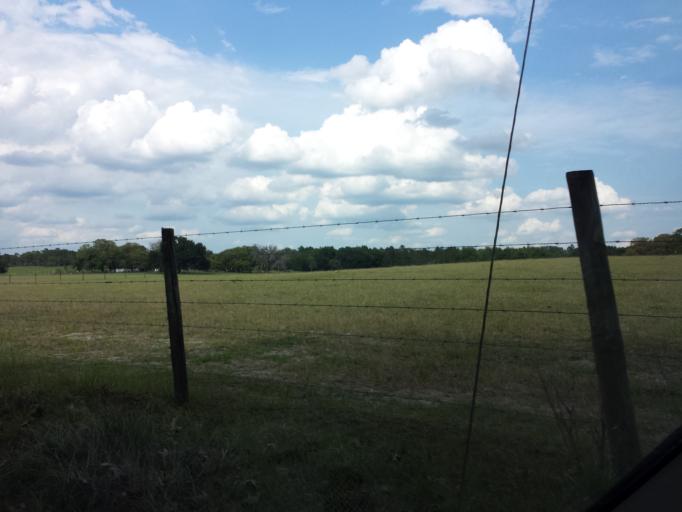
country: US
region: Florida
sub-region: Hernando County
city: Hill 'n Dale
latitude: 28.5364
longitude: -82.2842
